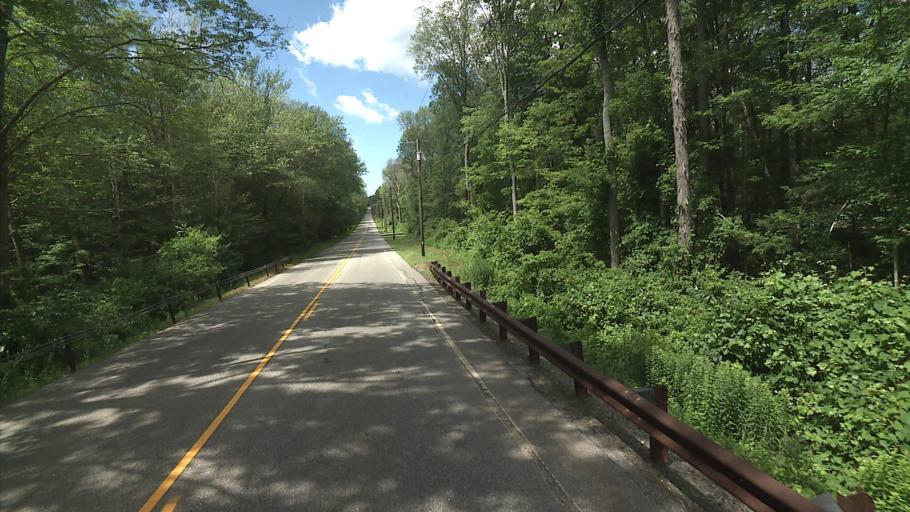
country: US
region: Connecticut
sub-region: New London County
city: Old Mystic
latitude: 41.4099
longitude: -71.9214
